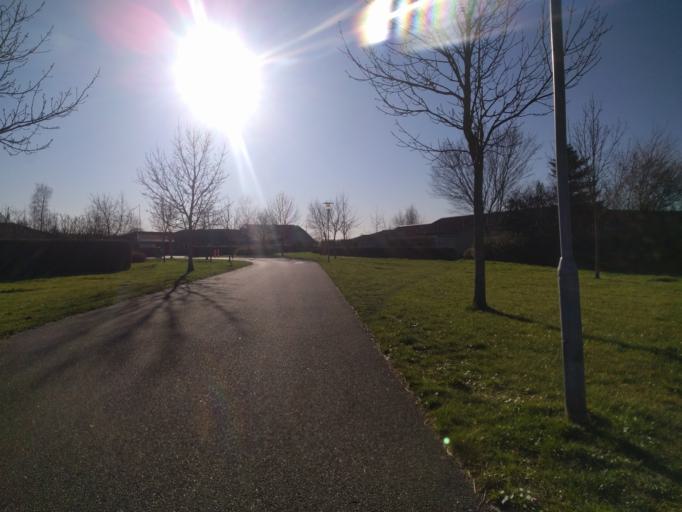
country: DK
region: South Denmark
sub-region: Odense Kommune
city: Bullerup
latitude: 55.3888
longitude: 10.5218
